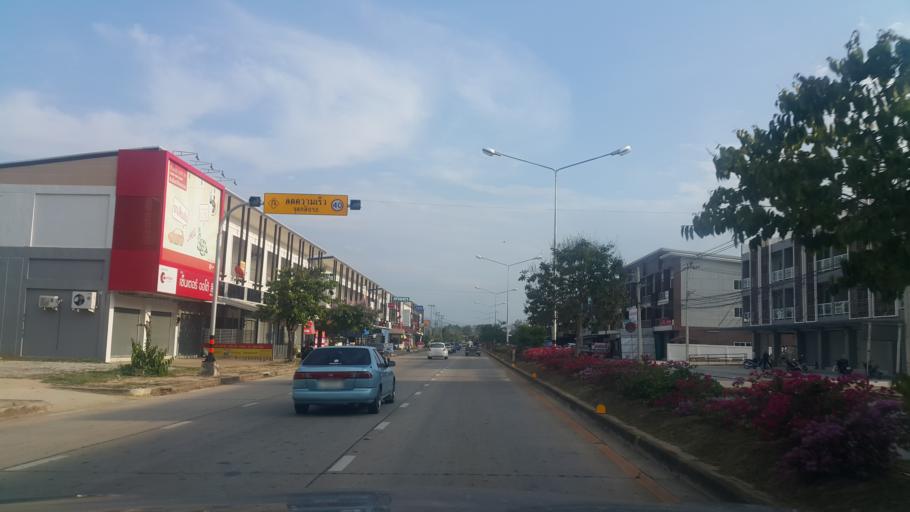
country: TH
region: Chiang Rai
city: Chiang Rai
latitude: 19.9163
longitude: 99.8603
